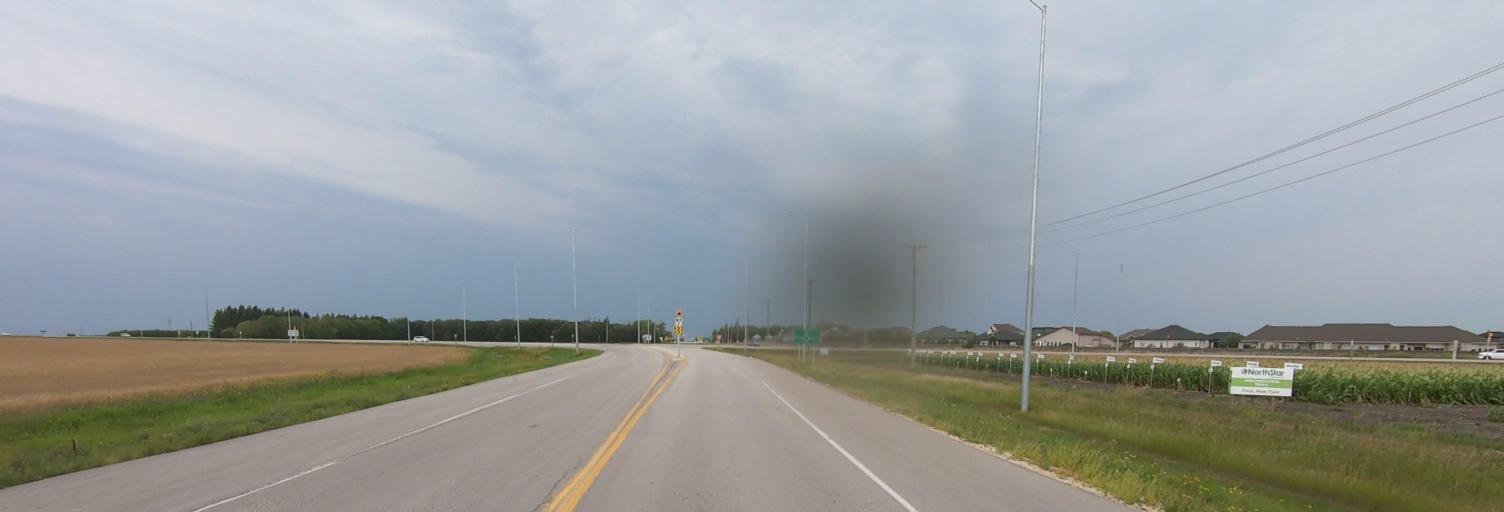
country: CA
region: Manitoba
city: Headingley
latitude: 49.7684
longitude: -97.3253
